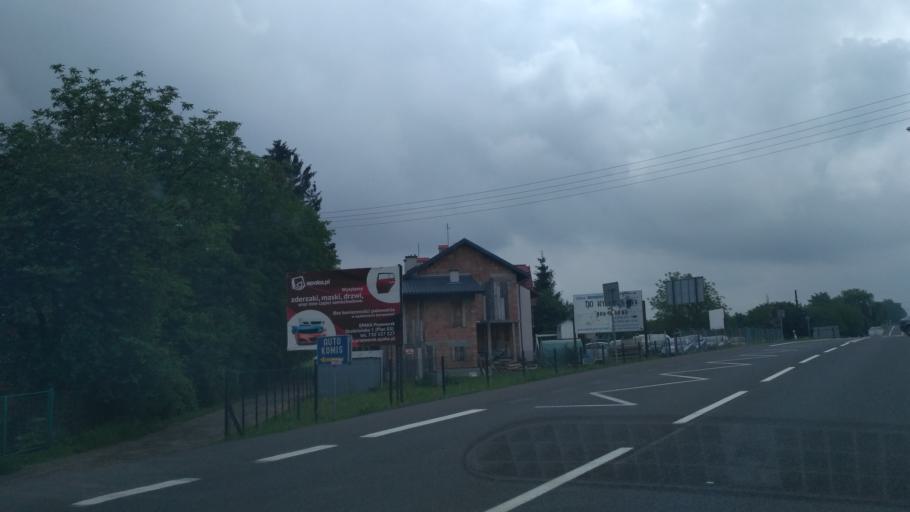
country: PL
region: Subcarpathian Voivodeship
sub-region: Powiat przeworski
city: Przeworsk
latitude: 50.0567
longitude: 22.5043
